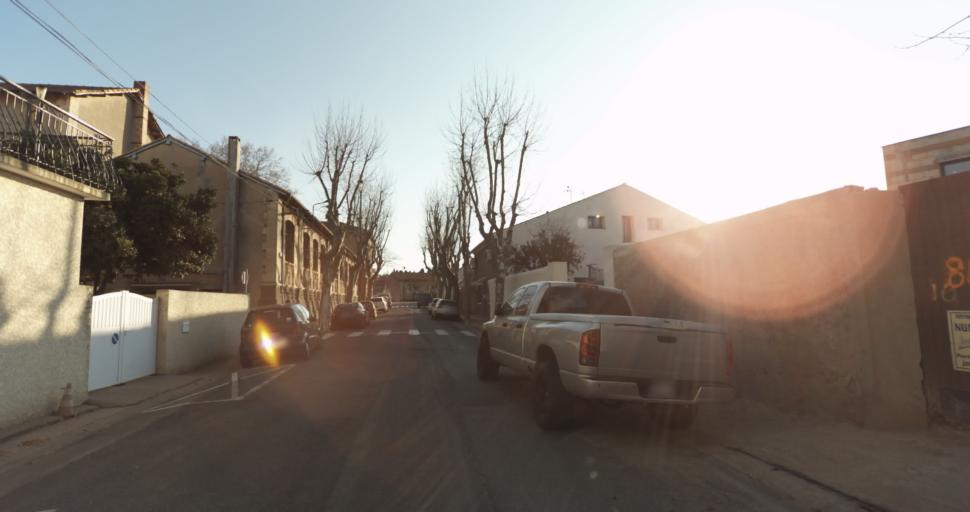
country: FR
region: Languedoc-Roussillon
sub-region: Departement de l'Herault
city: Marseillan
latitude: 43.3584
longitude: 3.5269
